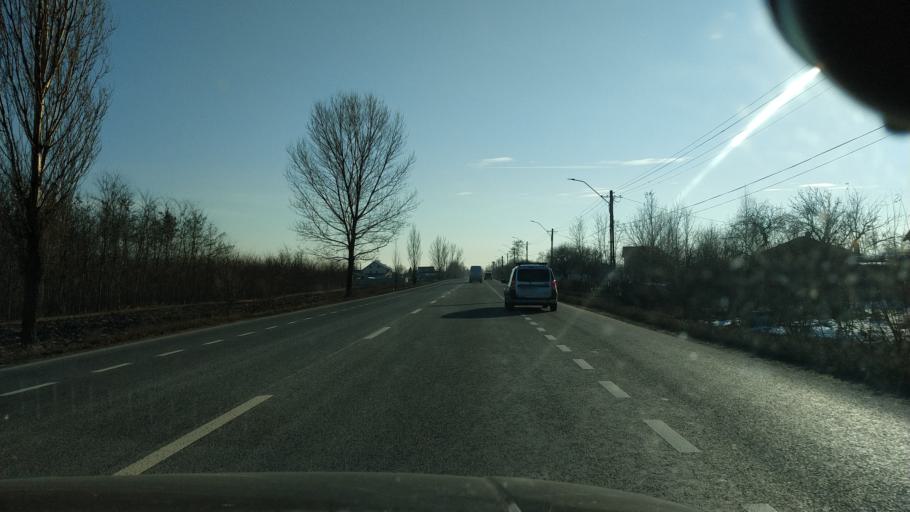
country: RO
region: Neamt
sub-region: Comuna Icusesti
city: Icusesti
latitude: 46.8205
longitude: 26.8855
